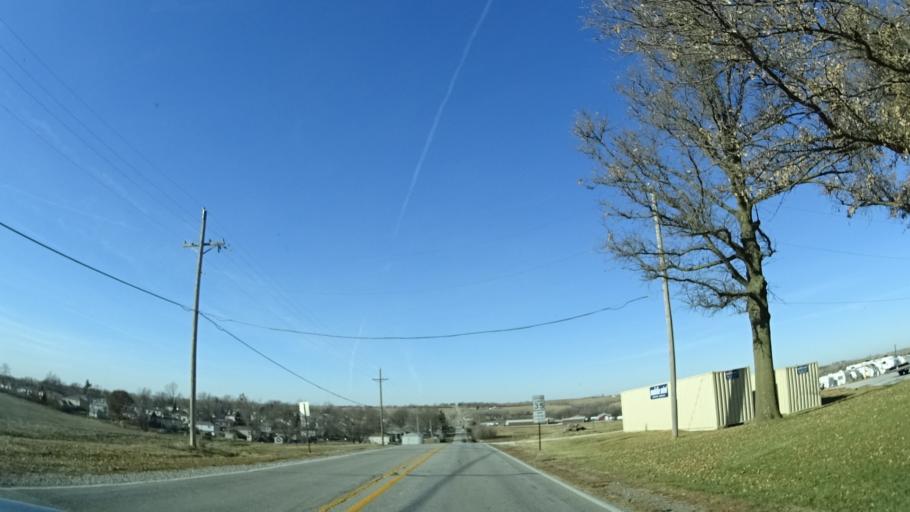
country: US
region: Nebraska
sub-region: Sarpy County
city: Springfield
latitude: 41.0891
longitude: -96.1263
